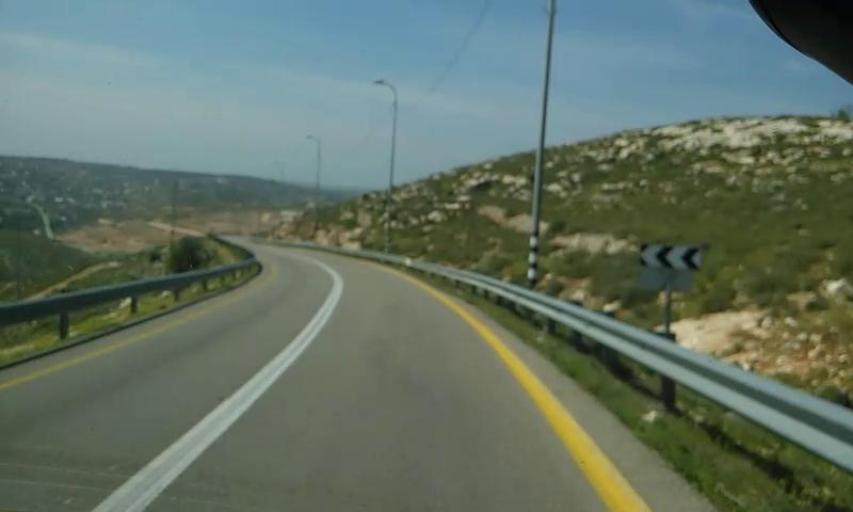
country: PS
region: West Bank
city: Surif
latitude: 31.6701
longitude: 35.0782
